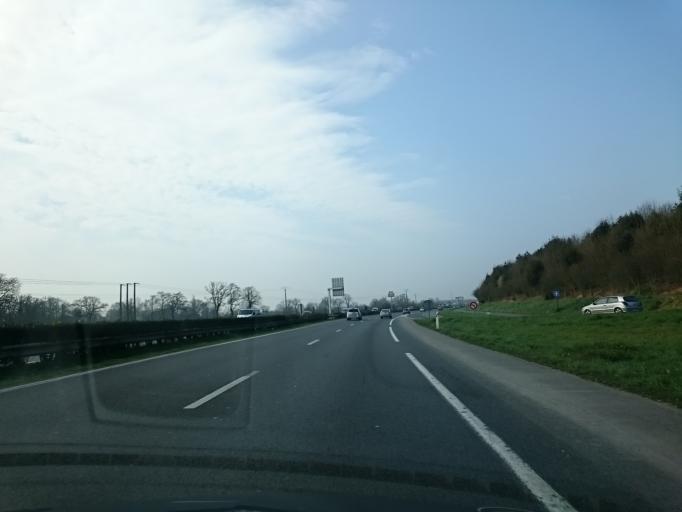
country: FR
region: Brittany
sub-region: Departement d'Ille-et-Vilaine
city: Chantepie
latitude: 48.0825
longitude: -1.6455
